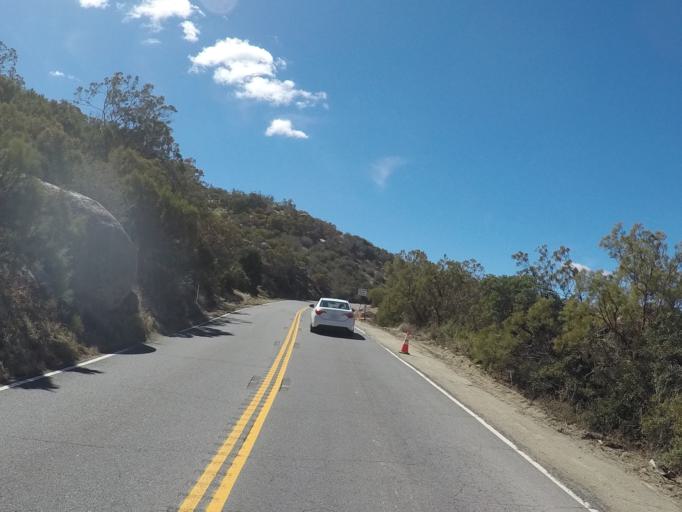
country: US
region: California
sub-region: Riverside County
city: Idyllwild-Pine Cove
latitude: 33.7035
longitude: -116.7672
